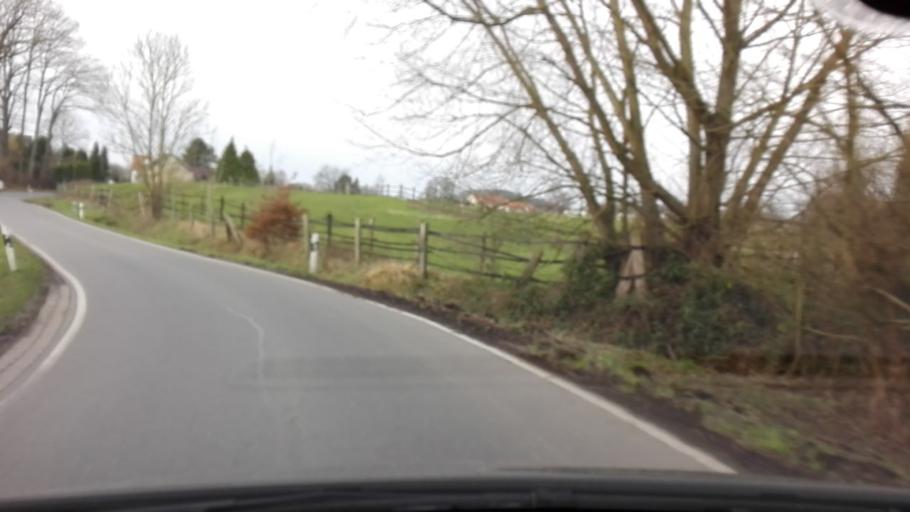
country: DE
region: North Rhine-Westphalia
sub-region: Regierungsbezirk Arnsberg
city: Holzwickede
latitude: 51.4810
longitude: 7.6739
